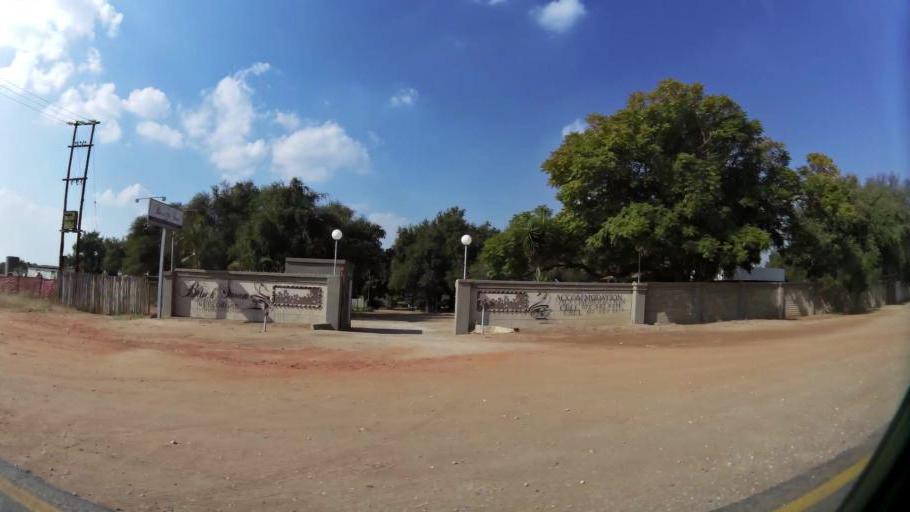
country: ZA
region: North-West
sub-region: Bojanala Platinum District Municipality
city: Rustenburg
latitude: -25.4863
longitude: 27.0861
